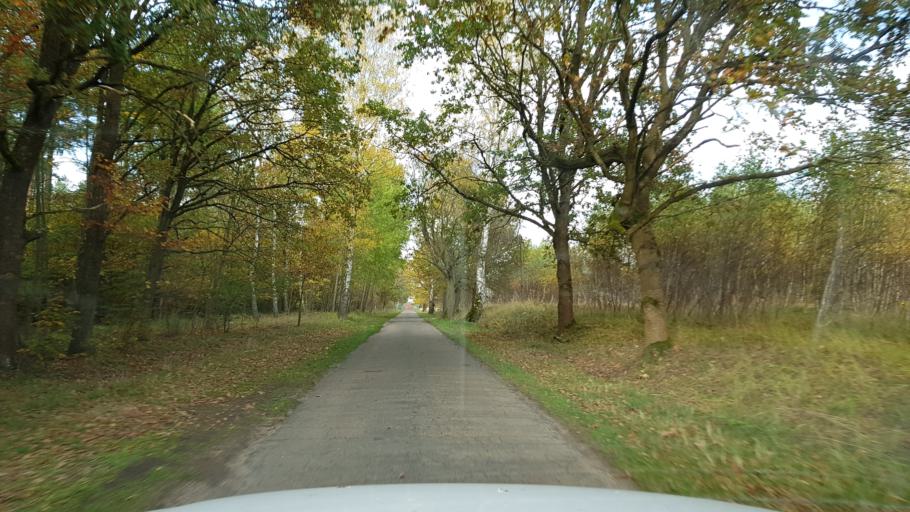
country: PL
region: West Pomeranian Voivodeship
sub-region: Powiat lobeski
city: Wegorzyno
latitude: 53.5124
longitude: 15.4963
